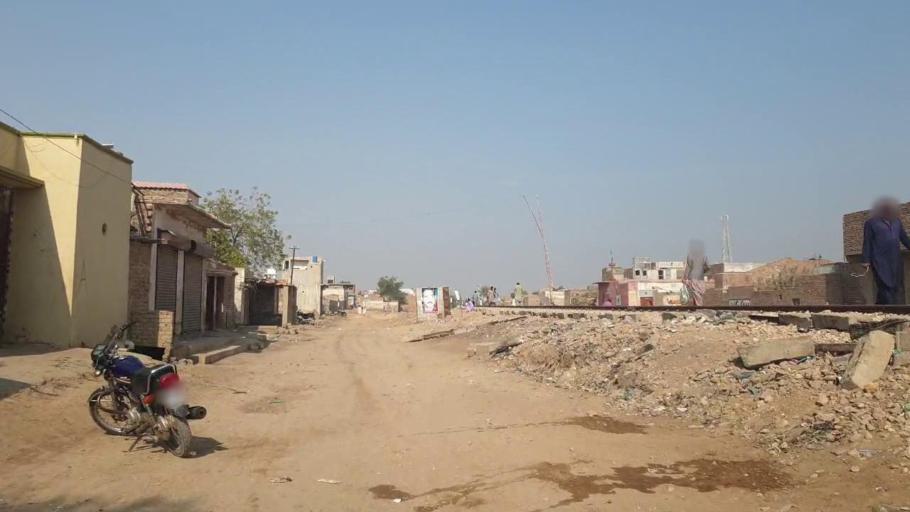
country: PK
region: Sindh
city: Jamshoro
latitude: 25.4328
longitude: 68.2803
